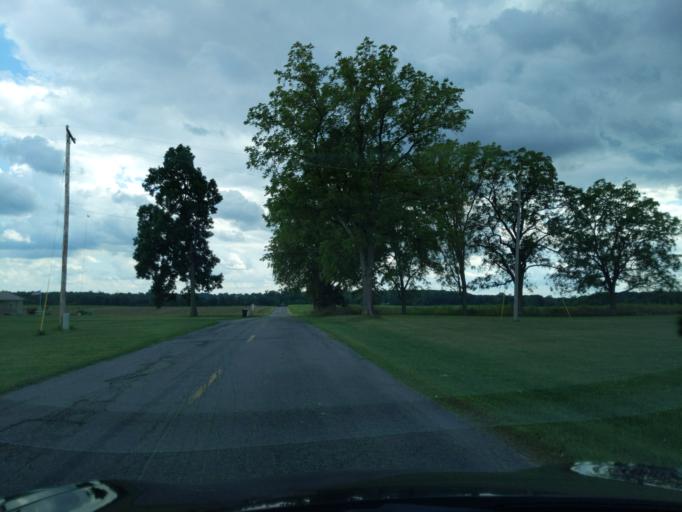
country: US
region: Michigan
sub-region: Eaton County
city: Eaton Rapids
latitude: 42.4436
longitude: -84.5803
